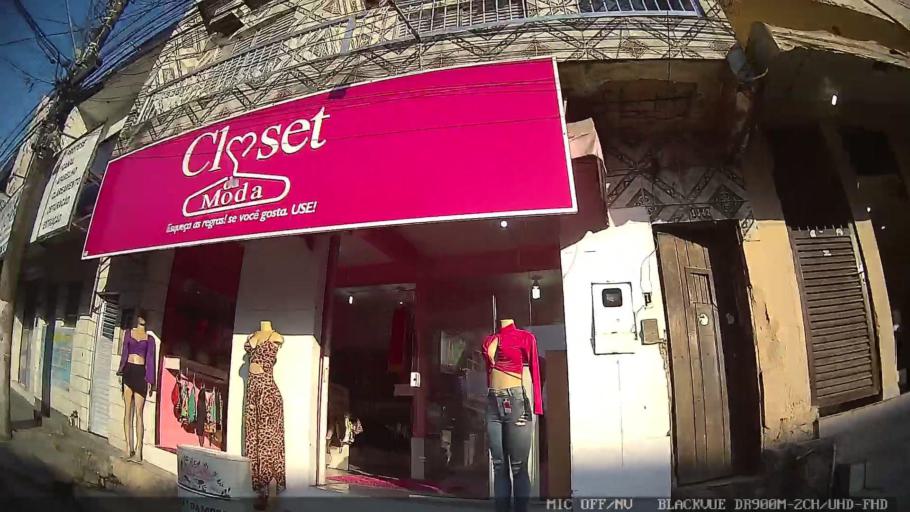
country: BR
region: Sao Paulo
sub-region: Guaruja
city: Guaruja
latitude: -23.9765
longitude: -46.2576
